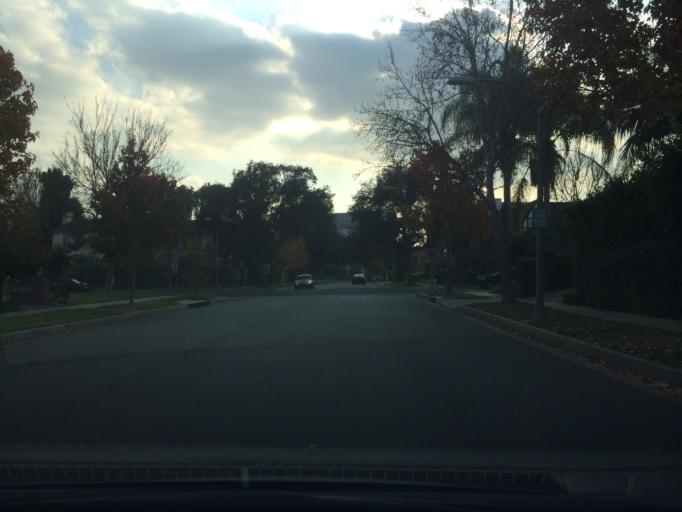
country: US
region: California
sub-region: Los Angeles County
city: Beverly Hills
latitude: 34.0703
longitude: -118.4106
